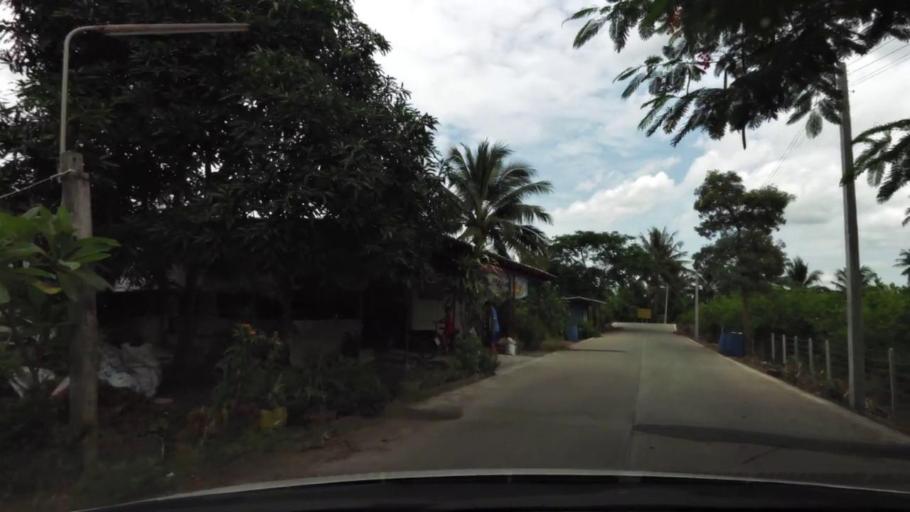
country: TH
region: Samut Sakhon
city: Ban Phaeo
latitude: 13.5649
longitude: 100.0362
